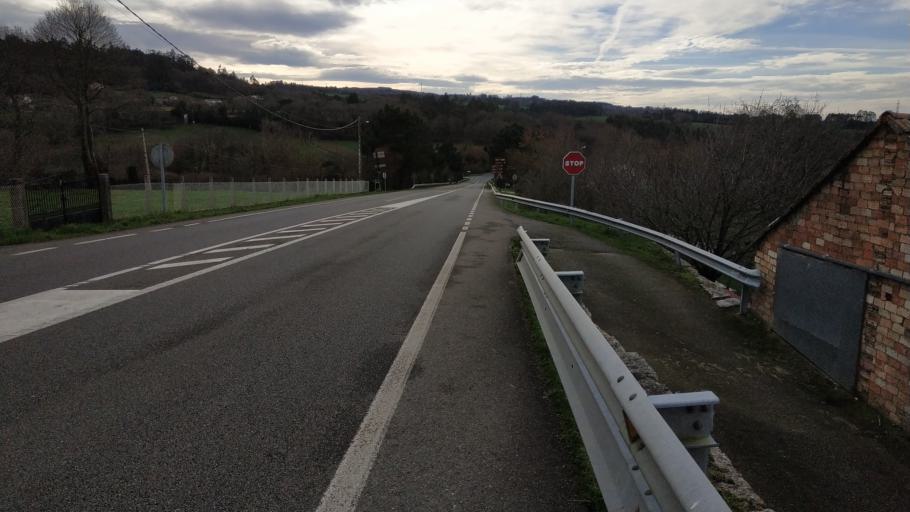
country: ES
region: Galicia
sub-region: Provincia de Pontevedra
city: Silleda
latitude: 42.7837
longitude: -8.1705
